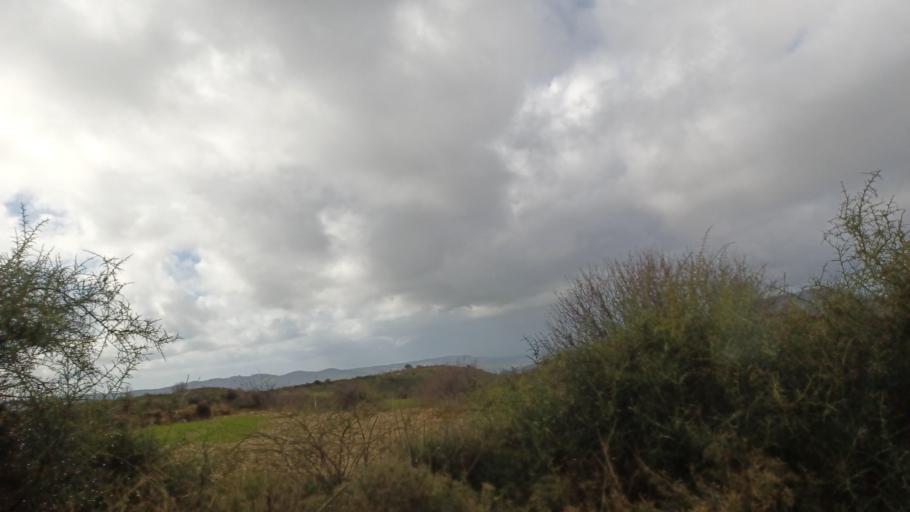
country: CY
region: Limassol
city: Pachna
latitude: 34.8308
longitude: 32.7440
